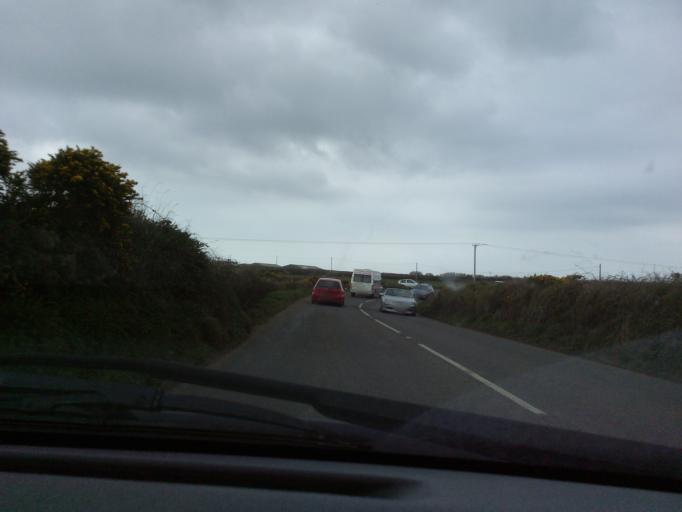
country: GB
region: England
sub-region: Cornwall
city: Sennen
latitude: 50.0840
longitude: -5.6767
